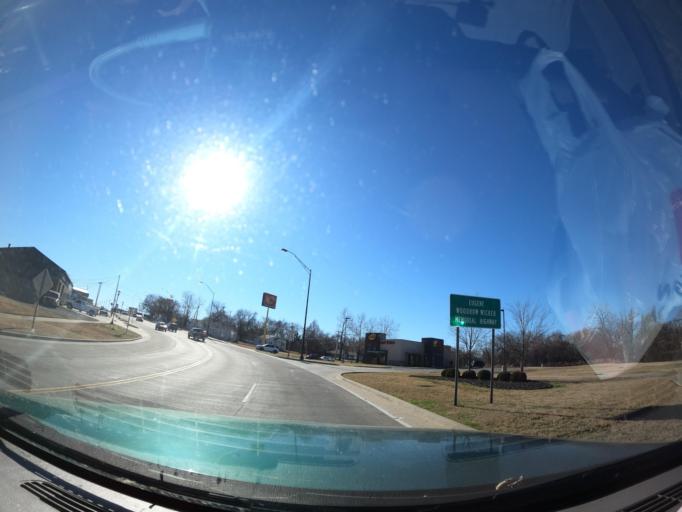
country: US
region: Oklahoma
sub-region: Wagoner County
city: Coweta
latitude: 35.9559
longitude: -95.6504
